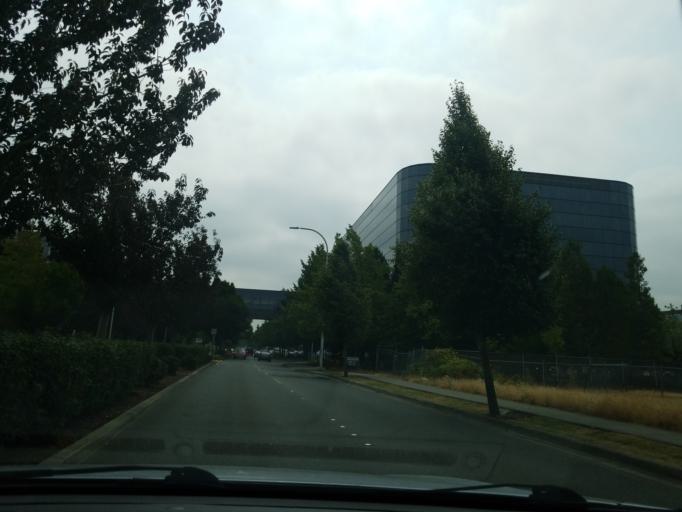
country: US
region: Washington
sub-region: King County
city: Renton
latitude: 47.4945
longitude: -122.2023
